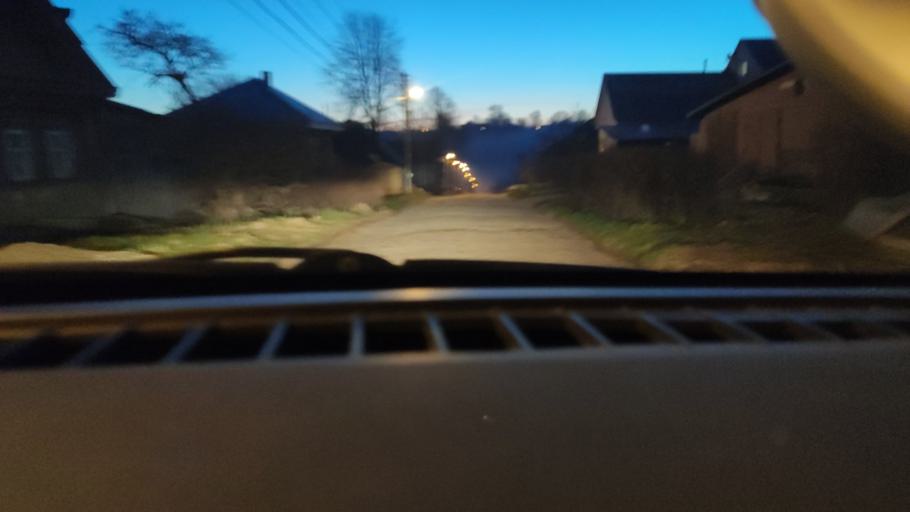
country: RU
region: Perm
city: Perm
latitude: 58.0408
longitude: 56.3347
